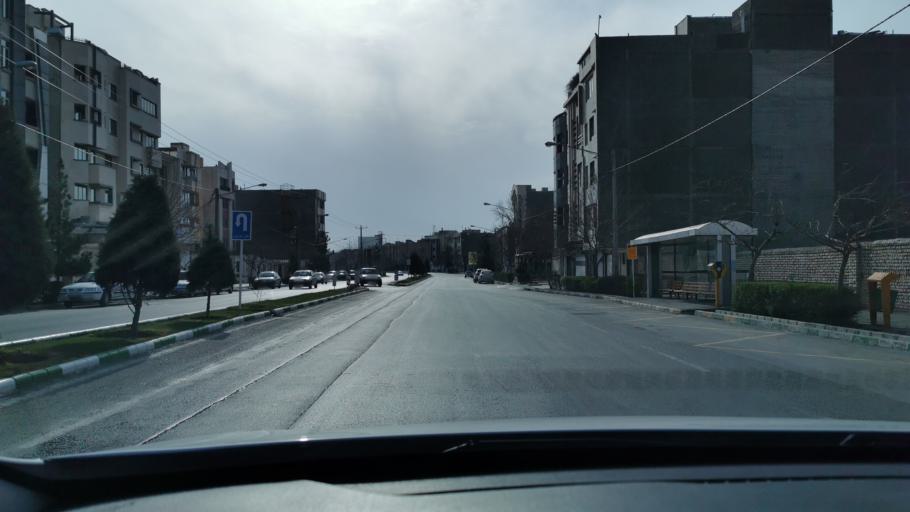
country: IR
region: Razavi Khorasan
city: Mashhad
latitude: 36.3151
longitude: 59.5102
